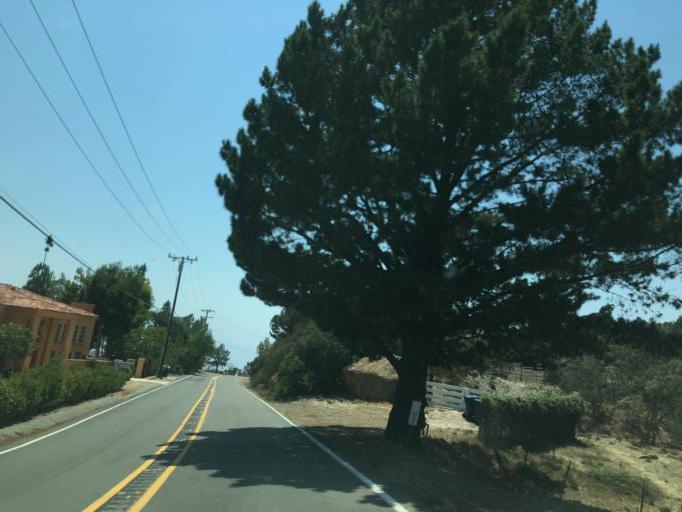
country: US
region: California
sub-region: Los Angeles County
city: Las Flores
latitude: 34.0776
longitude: -118.6436
